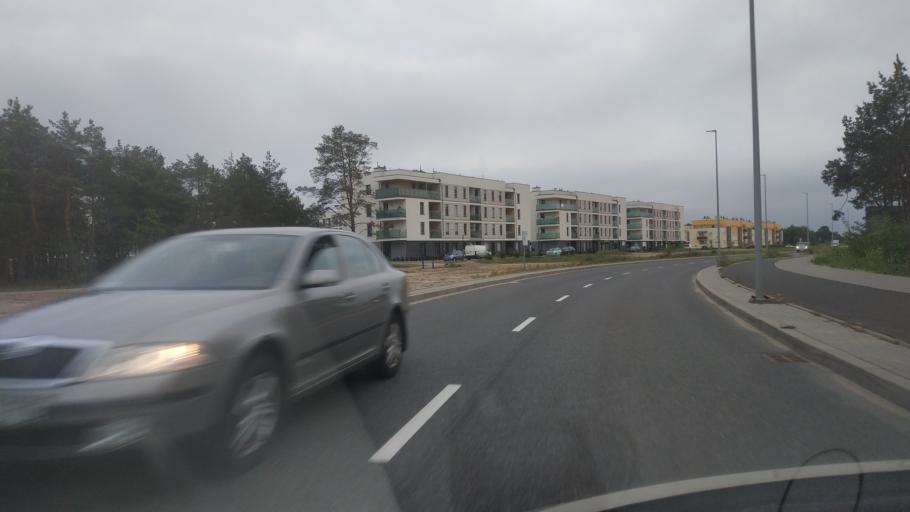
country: PL
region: Kujawsko-Pomorskie
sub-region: Torun
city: Torun
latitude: 53.0488
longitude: 18.6045
